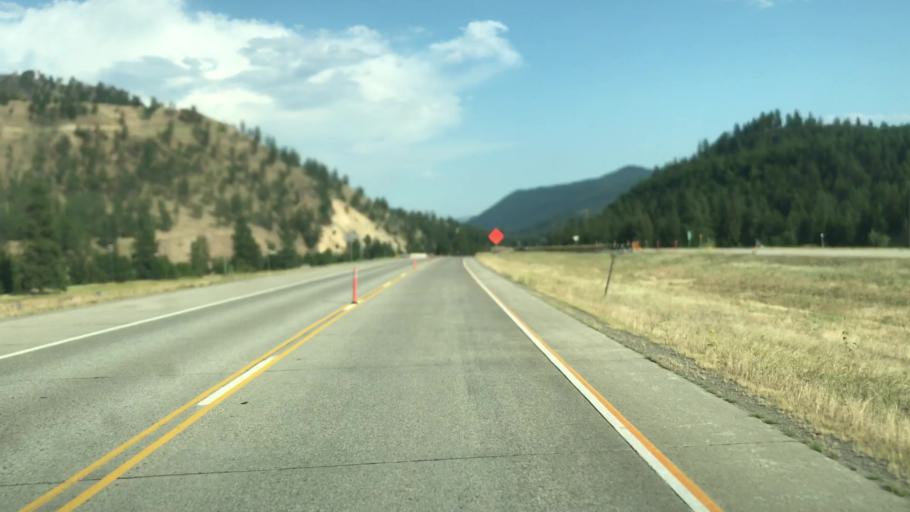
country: US
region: Montana
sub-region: Mineral County
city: Superior
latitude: 47.2265
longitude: -114.9697
